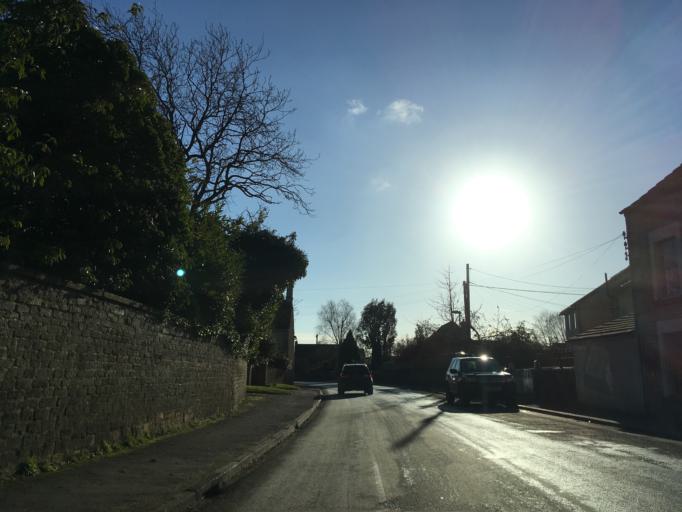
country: GB
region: England
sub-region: Wiltshire
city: Biddestone
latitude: 51.4863
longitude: -2.1933
